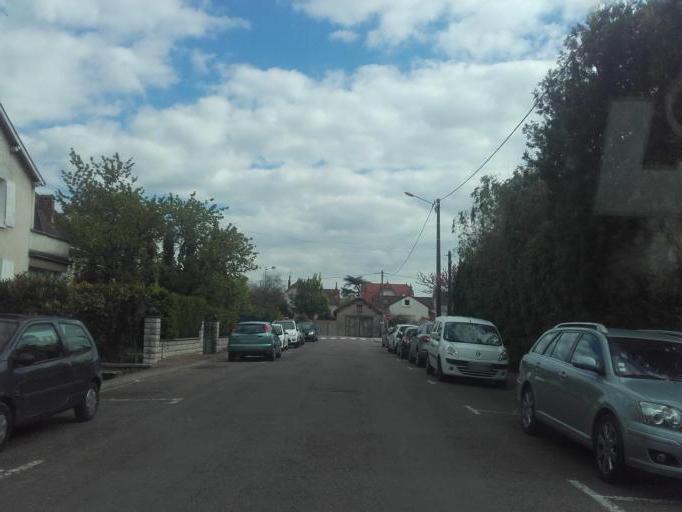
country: FR
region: Bourgogne
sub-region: Departement de la Cote-d'Or
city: Nuits-Saint-Georges
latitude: 47.1359
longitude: 4.9521
